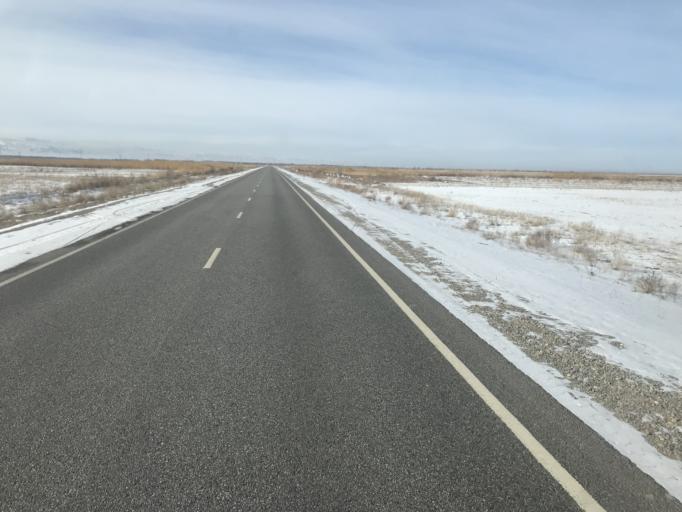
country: KZ
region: Zhambyl
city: Taraz
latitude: 43.0085
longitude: 71.2804
